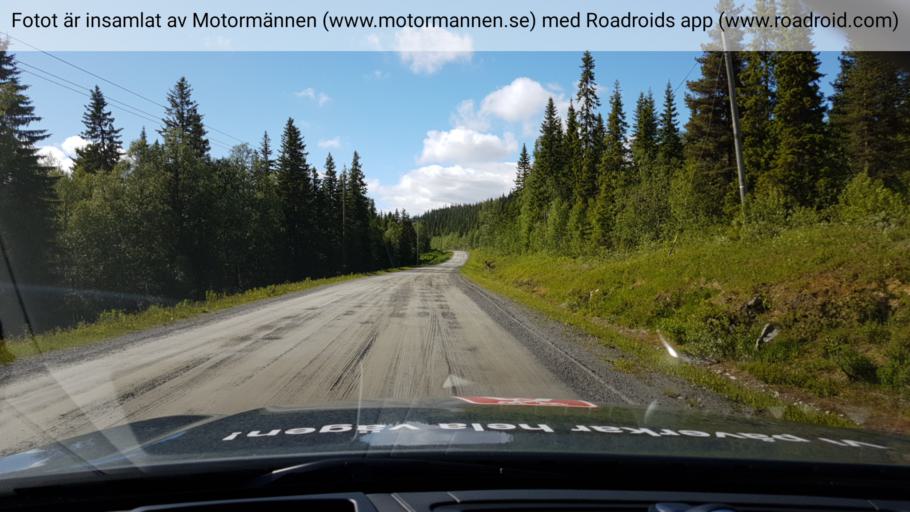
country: SE
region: Jaemtland
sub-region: Are Kommun
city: Are
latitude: 63.6916
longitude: 12.8034
